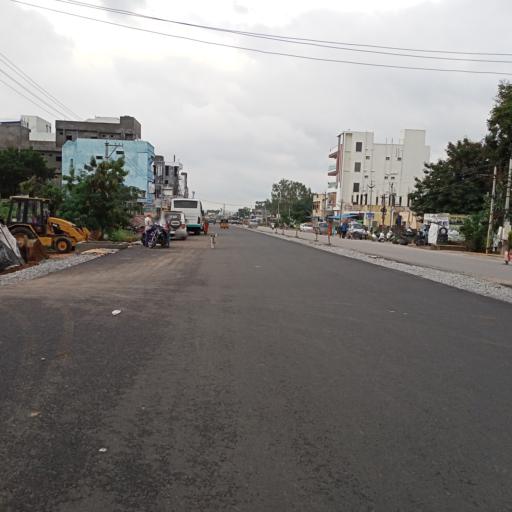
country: IN
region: Telangana
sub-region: Mahbubnagar
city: Mahbubnagar
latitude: 16.7741
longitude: 78.1254
